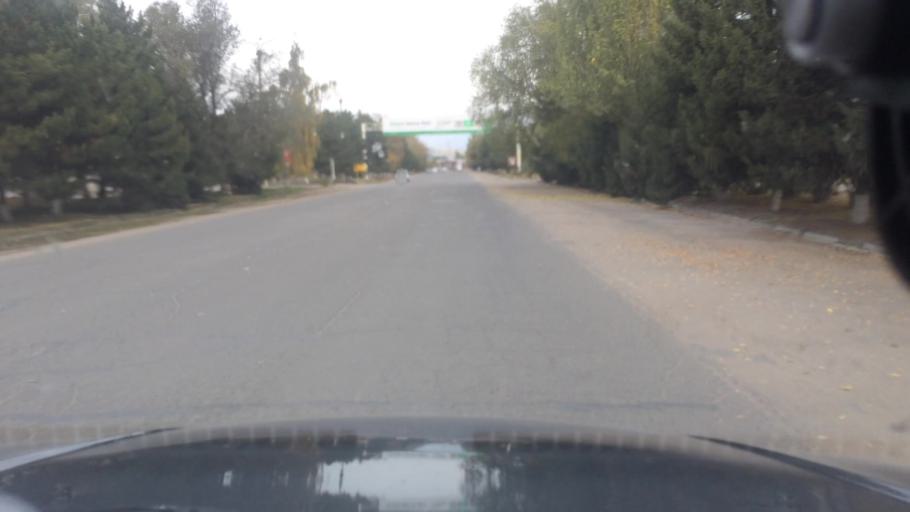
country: KG
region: Ysyk-Koel
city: Karakol
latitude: 42.4961
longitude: 78.3916
